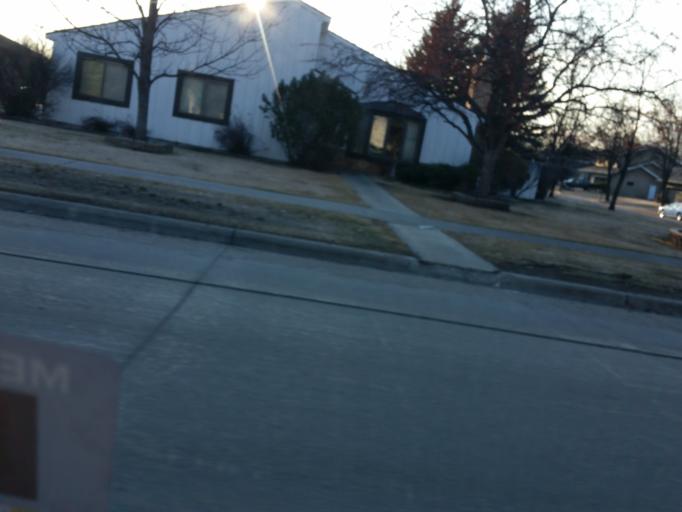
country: US
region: North Dakota
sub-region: Grand Forks County
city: Grand Forks
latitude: 47.8762
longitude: -97.0292
